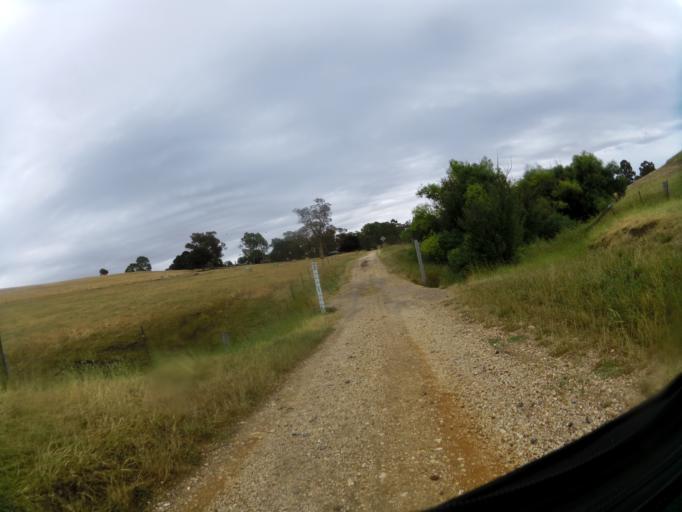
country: AU
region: Victoria
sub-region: Mount Alexander
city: Castlemaine
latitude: -37.2016
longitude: 144.0163
